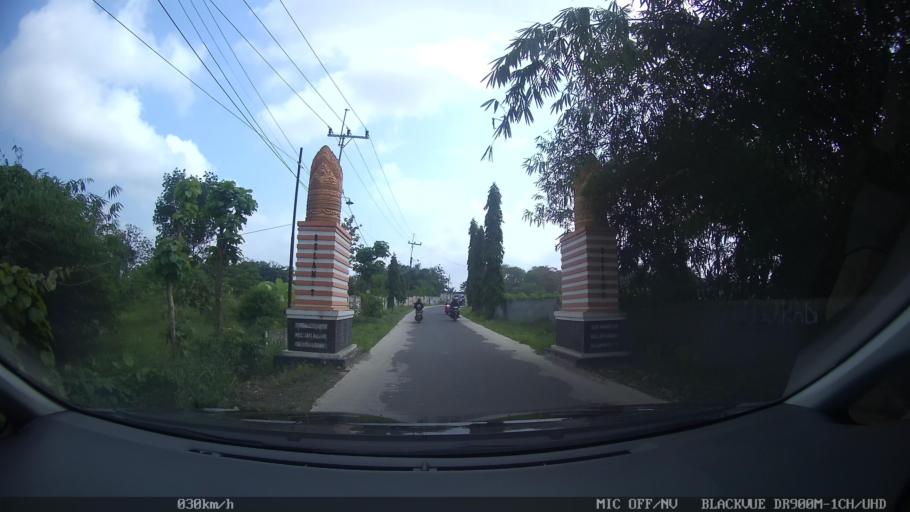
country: ID
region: Lampung
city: Kedaton
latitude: -5.3374
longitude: 105.2769
